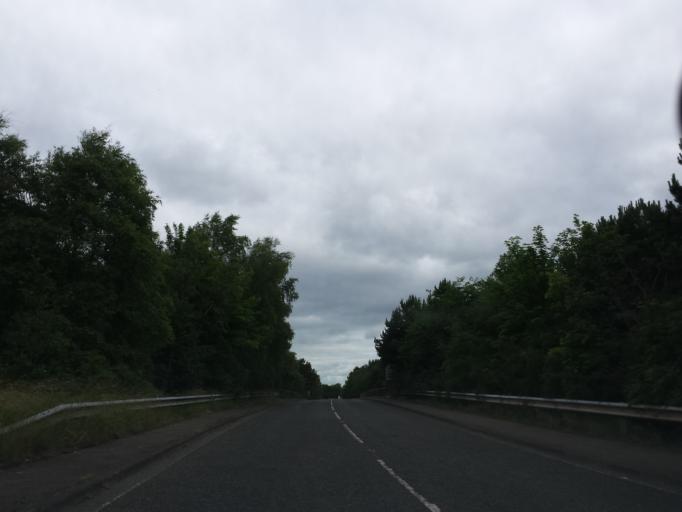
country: GB
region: Scotland
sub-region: East Lothian
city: Musselburgh
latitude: 55.9265
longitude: -3.0374
